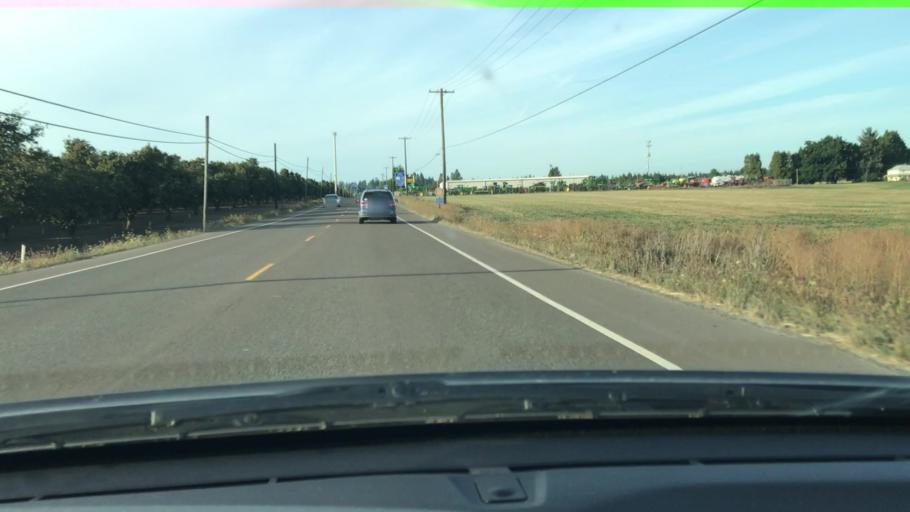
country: US
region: Oregon
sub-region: Yamhill County
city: McMinnville
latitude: 45.1845
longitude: -123.2100
